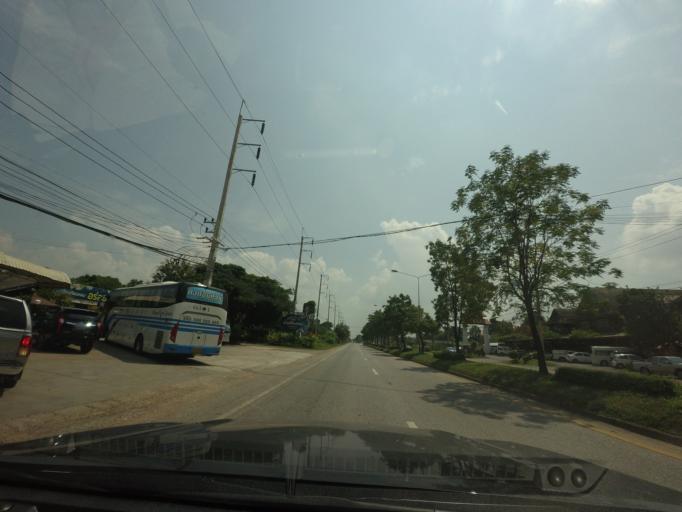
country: TH
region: Uttaradit
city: Uttaradit
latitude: 17.5938
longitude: 100.1305
